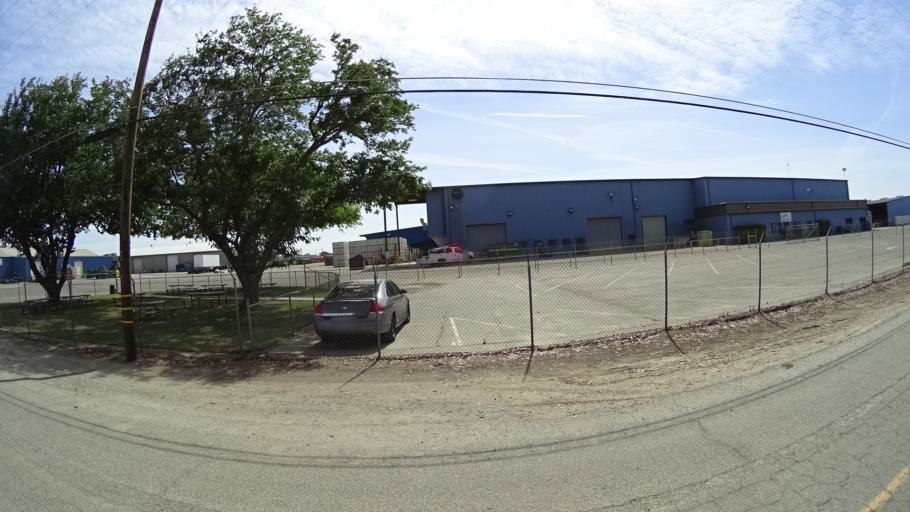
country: US
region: California
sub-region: Kings County
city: Hanford
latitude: 36.3262
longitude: -119.6258
